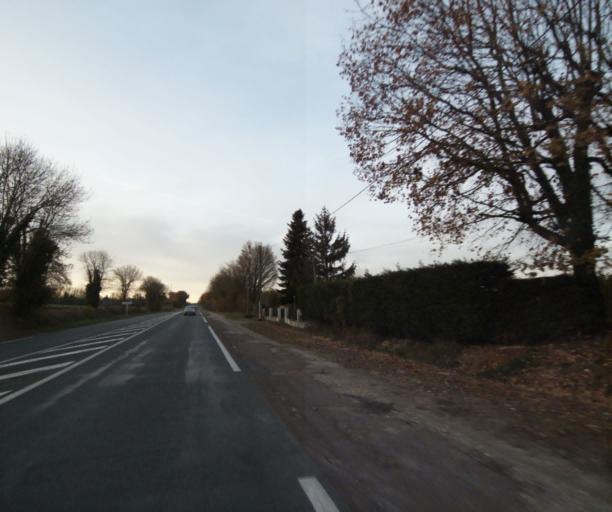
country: FR
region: Poitou-Charentes
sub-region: Departement de la Charente-Maritime
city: Saint-Georges-des-Coteaux
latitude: 45.7654
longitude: -0.6767
